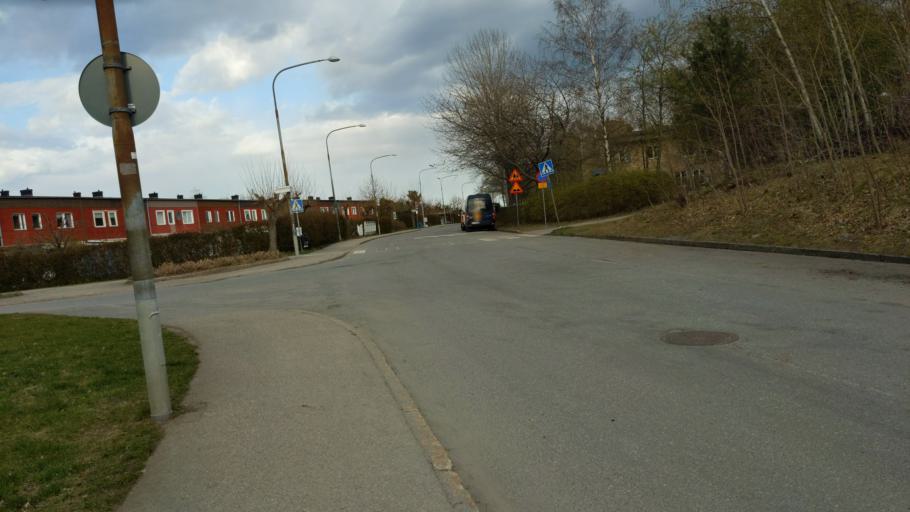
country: SE
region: Stockholm
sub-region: Stockholms Kommun
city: Kista
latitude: 59.3869
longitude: 17.8965
